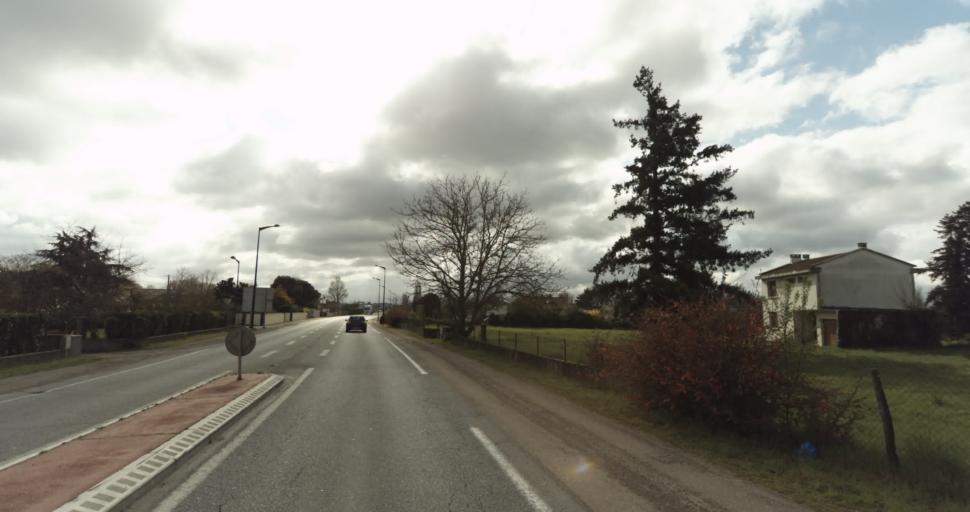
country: FR
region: Midi-Pyrenees
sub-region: Departement de la Haute-Garonne
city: Auterive
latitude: 43.3663
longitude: 1.4532
